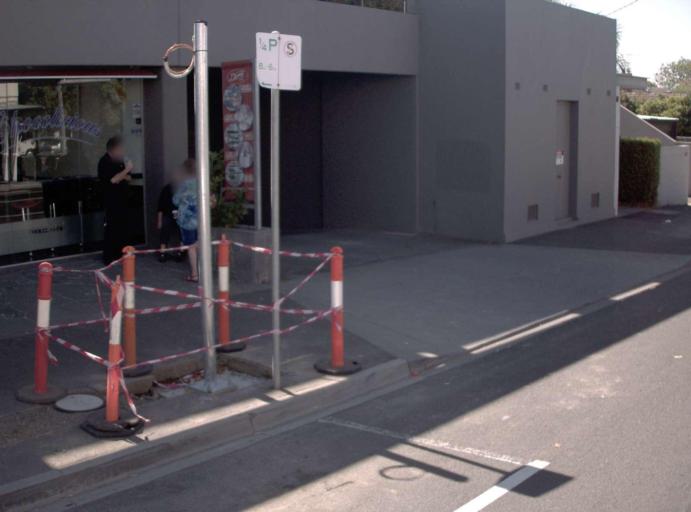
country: AU
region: Victoria
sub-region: Bayside
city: Hampton
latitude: -37.9285
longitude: 145.0042
